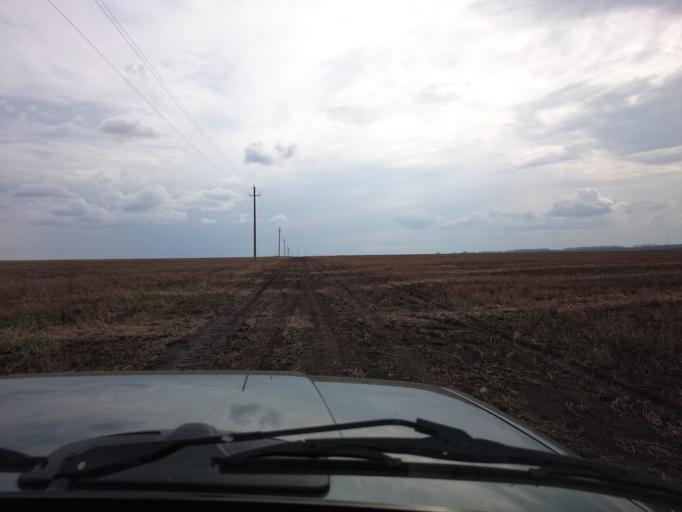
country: RU
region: Mordoviya
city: Kadoshkino
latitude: 54.0259
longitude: 44.4775
